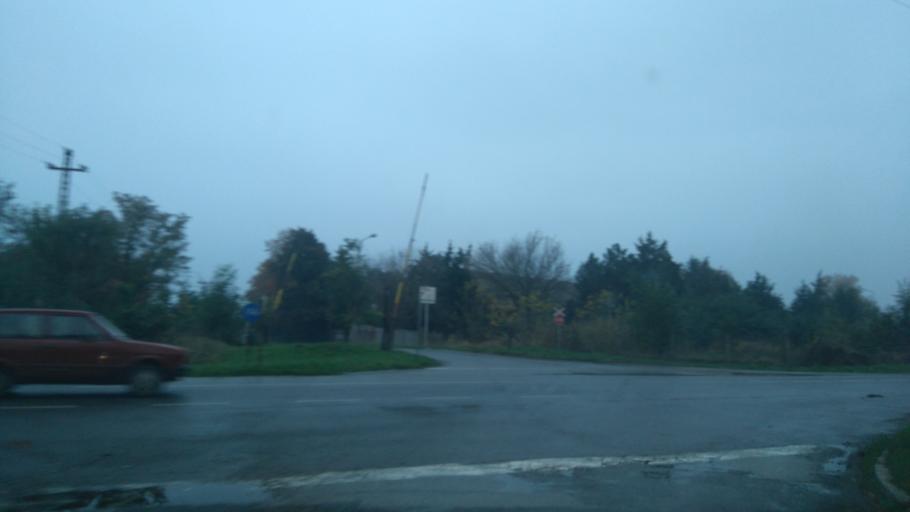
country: RS
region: Autonomna Pokrajina Vojvodina
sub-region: Juznobacki Okrug
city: Becej
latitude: 45.6280
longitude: 20.0354
